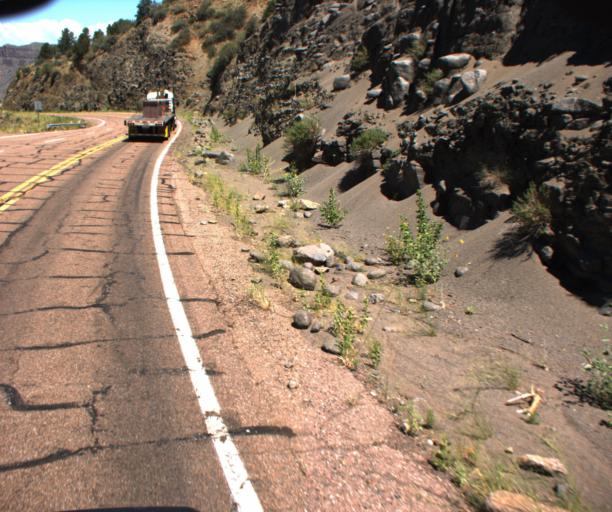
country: US
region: Arizona
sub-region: Navajo County
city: Cibecue
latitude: 33.7849
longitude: -110.5020
